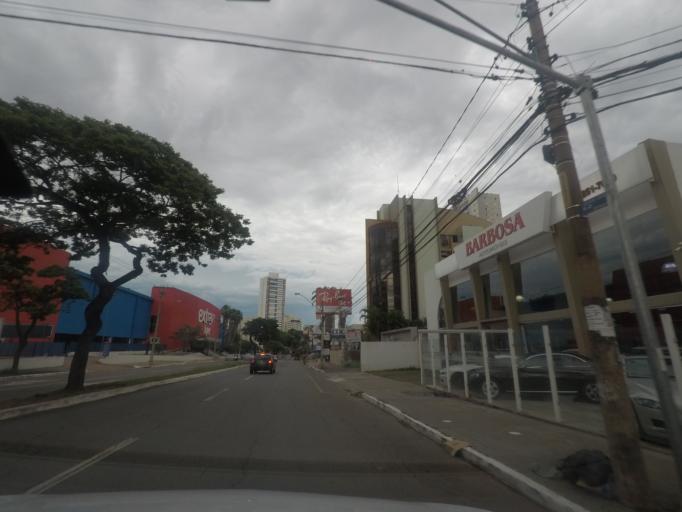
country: BR
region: Goias
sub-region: Goiania
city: Goiania
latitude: -16.6918
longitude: -49.2701
